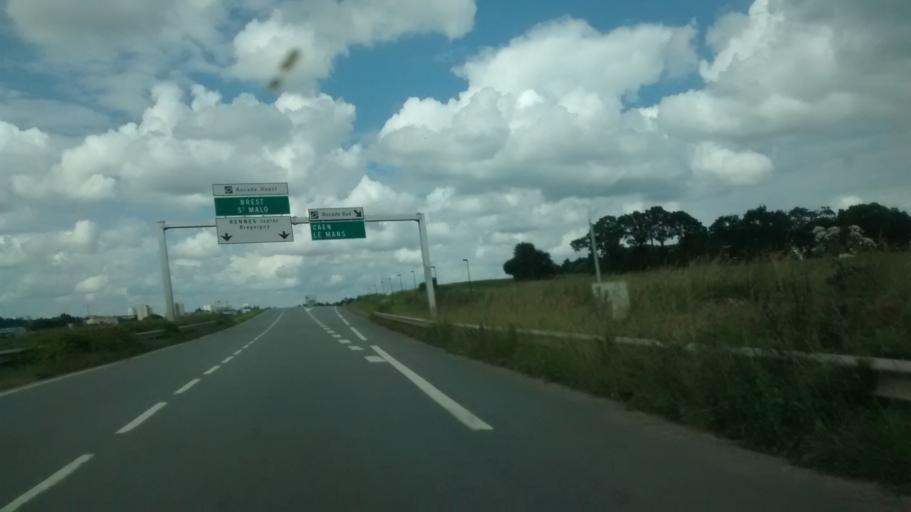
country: FR
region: Brittany
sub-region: Departement d'Ille-et-Vilaine
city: Saint-Jacques-de-la-Lande
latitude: 48.0722
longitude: -1.6965
